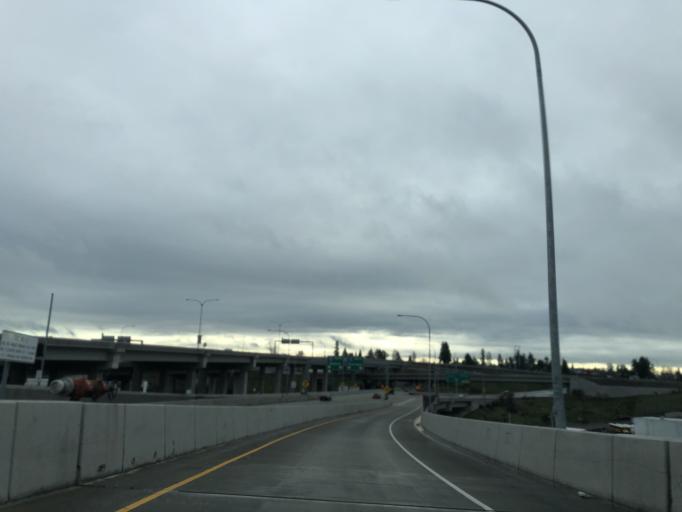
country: US
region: Washington
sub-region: Pierce County
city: Tacoma
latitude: 47.2337
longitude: -122.4648
